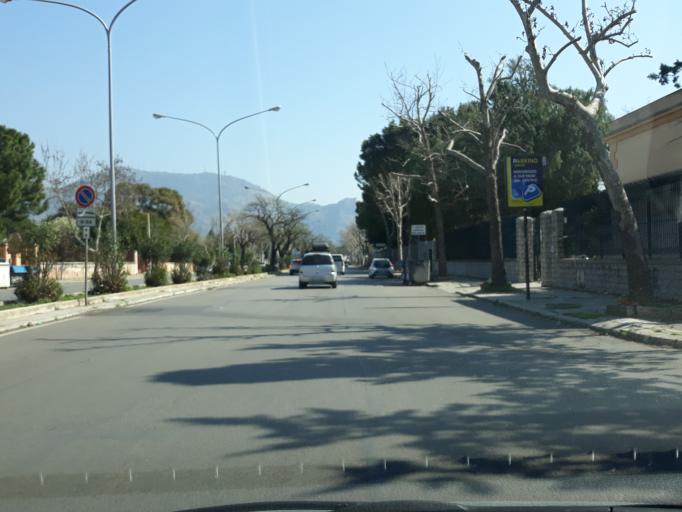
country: IT
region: Sicily
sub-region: Palermo
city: Palermo
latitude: 38.1349
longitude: 13.3137
